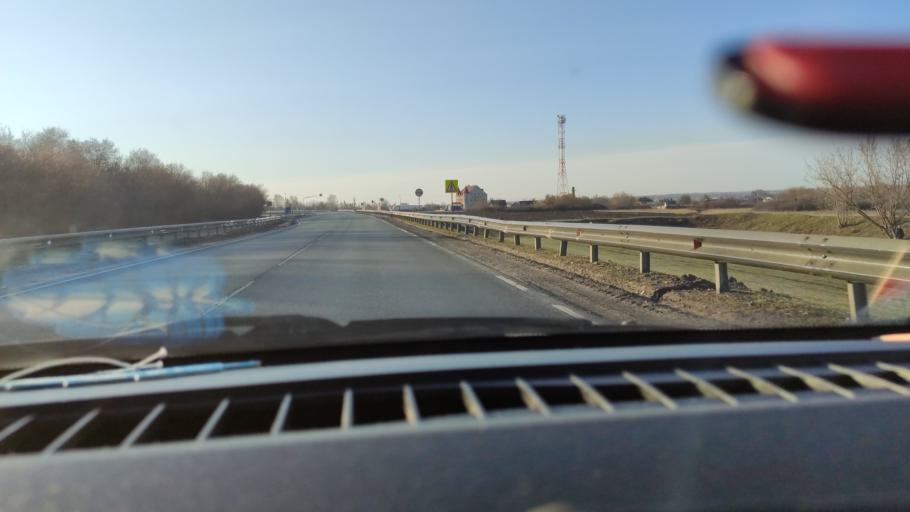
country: RU
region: Saratov
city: Tersa
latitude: 52.0857
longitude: 47.5515
